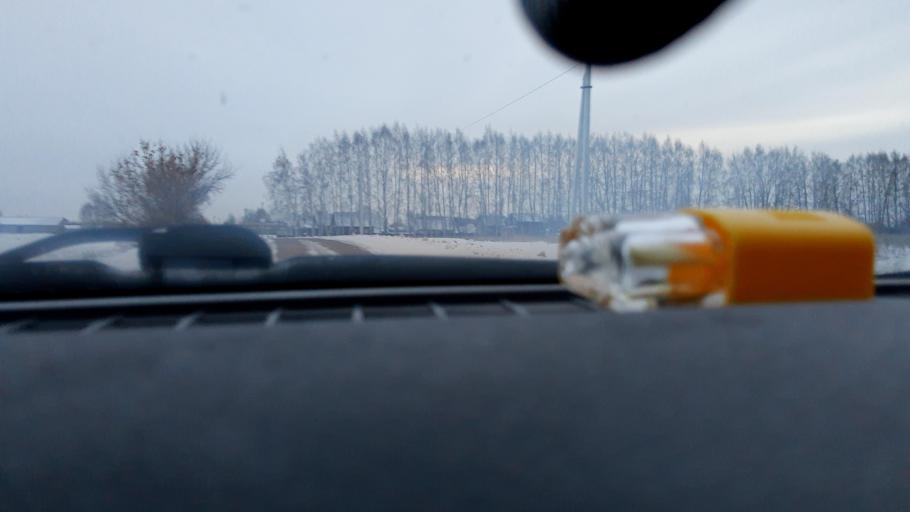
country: RU
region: Bashkortostan
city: Iglino
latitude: 54.8044
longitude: 56.4183
